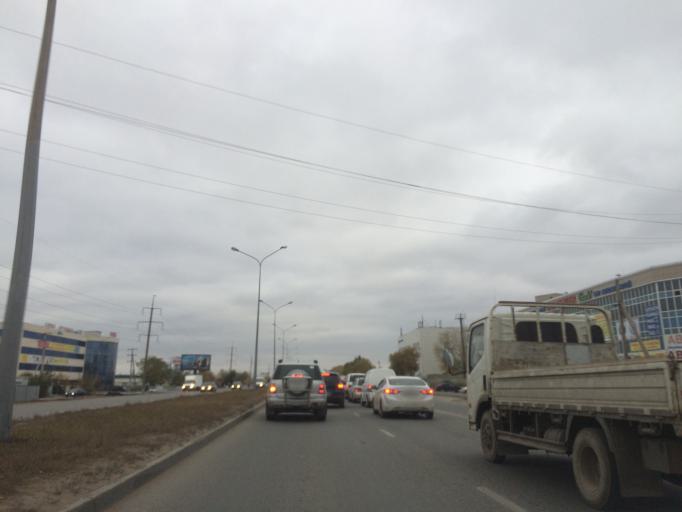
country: KZ
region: Astana Qalasy
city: Astana
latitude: 51.1923
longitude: 71.4626
